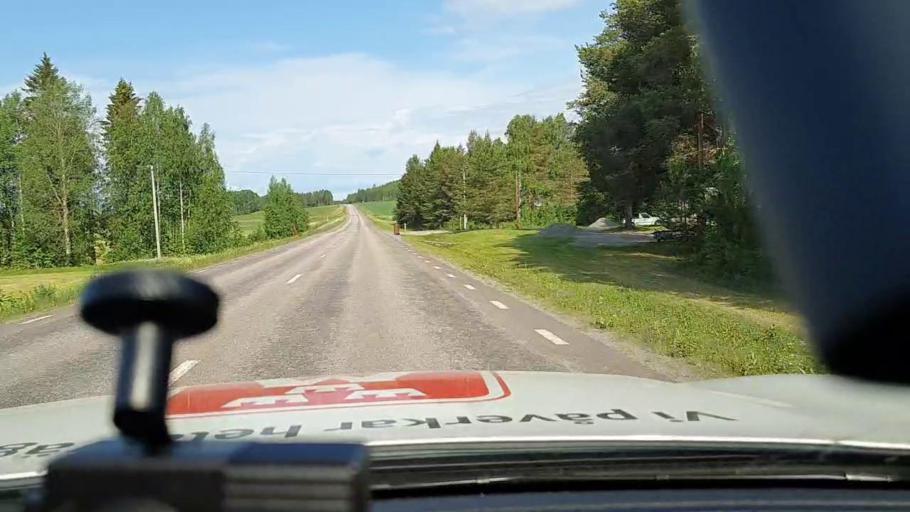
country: SE
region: Norrbotten
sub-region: Bodens Kommun
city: Boden
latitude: 65.9099
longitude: 21.3521
